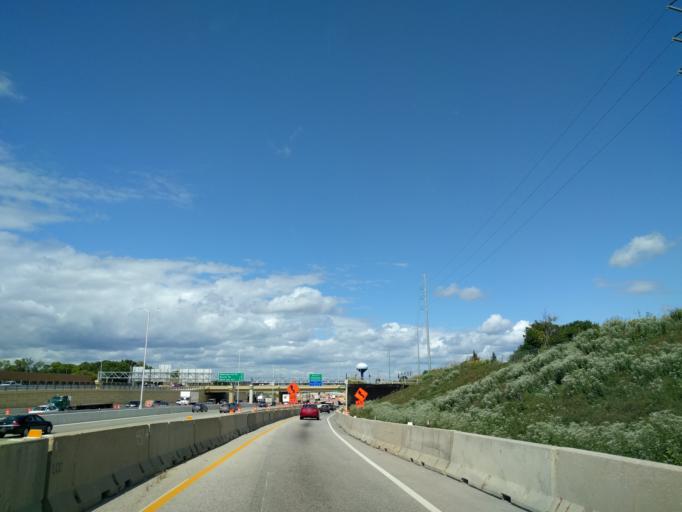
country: US
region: Wisconsin
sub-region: Milwaukee County
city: Wauwatosa
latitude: 43.0328
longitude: -88.0332
